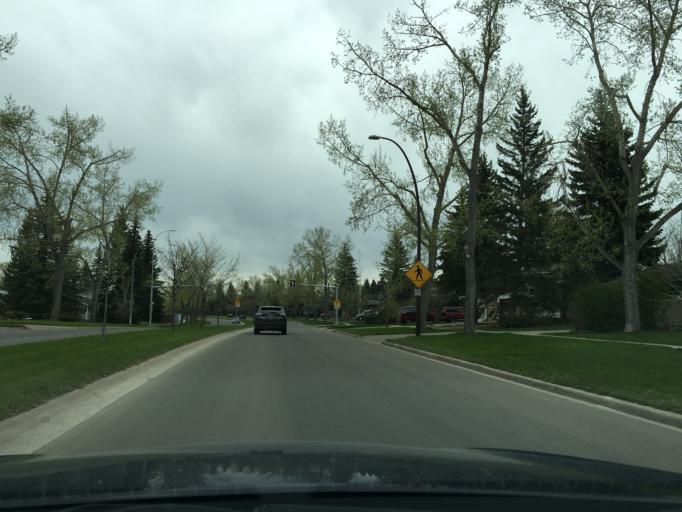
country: CA
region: Alberta
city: Calgary
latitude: 50.9429
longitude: -114.0614
